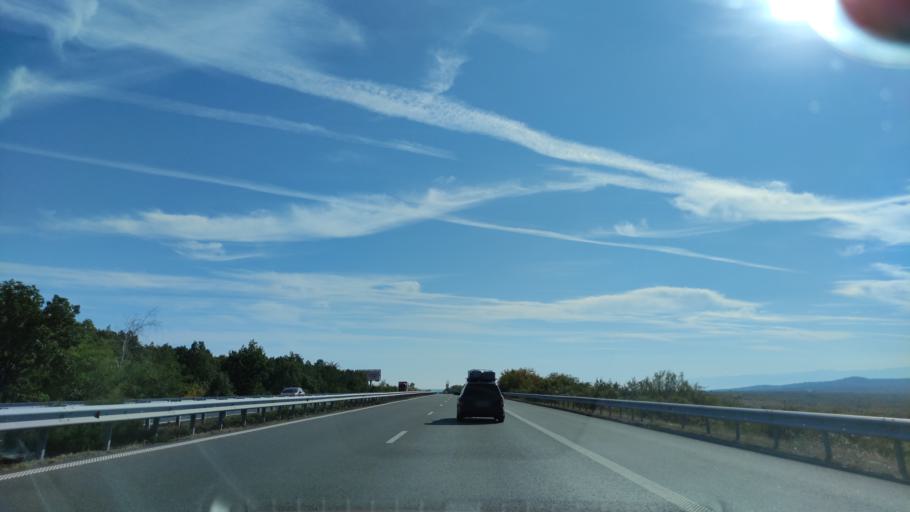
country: BG
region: Pazardzhik
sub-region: Obshtina Lesichevo
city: Lesichevo
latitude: 42.3188
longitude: 24.1344
